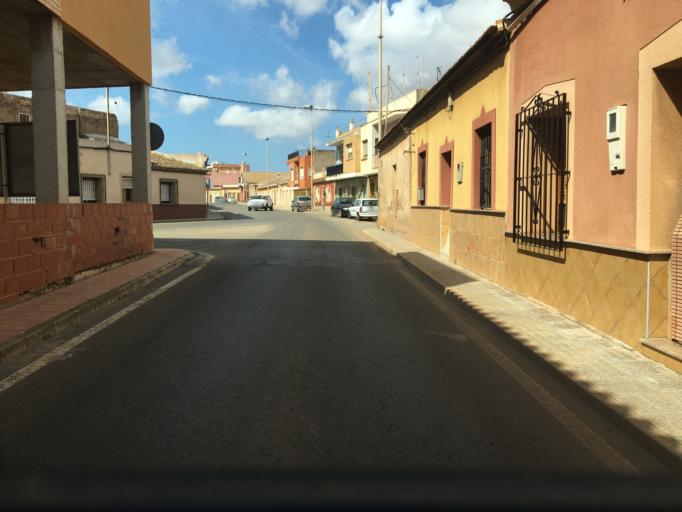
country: ES
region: Murcia
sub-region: Murcia
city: La Union
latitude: 37.6478
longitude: -0.8687
